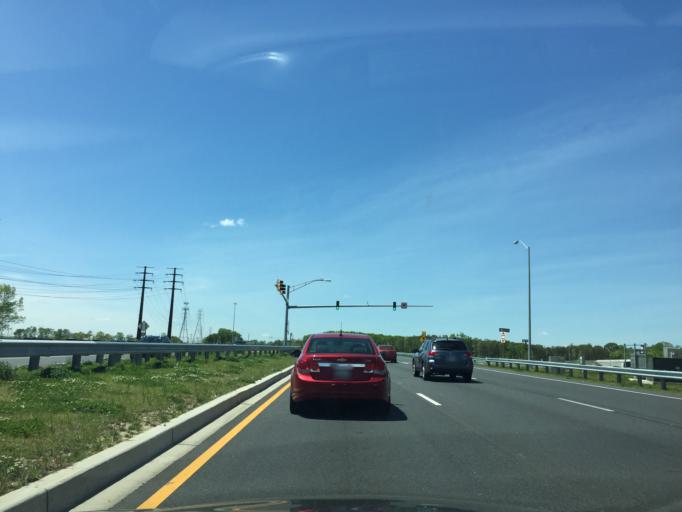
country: US
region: Maryland
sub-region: Baltimore County
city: White Marsh
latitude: 39.3787
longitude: -76.4448
